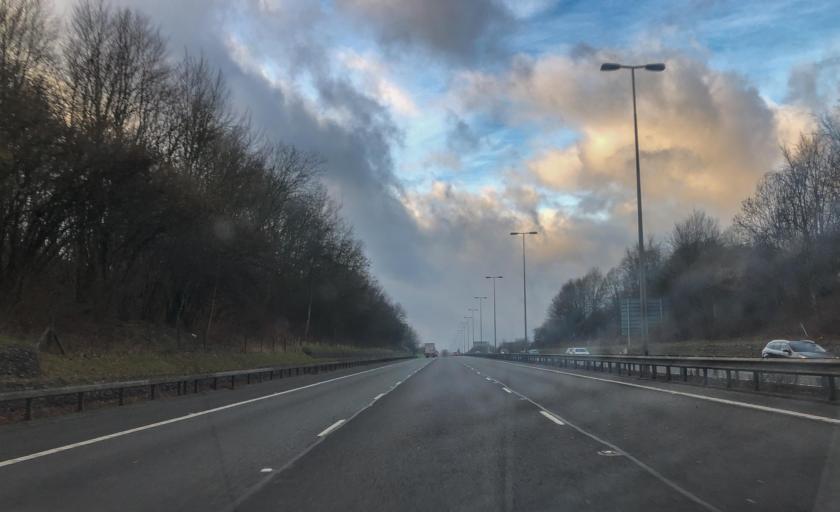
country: GB
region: England
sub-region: Buckinghamshire
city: Marlow
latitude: 51.6123
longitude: -0.7973
